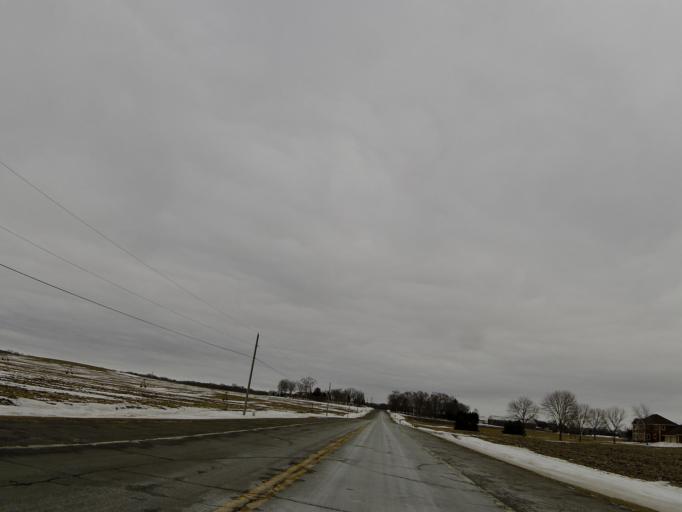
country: US
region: Minnesota
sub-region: Washington County
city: Cottage Grove
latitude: 44.8335
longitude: -92.9005
